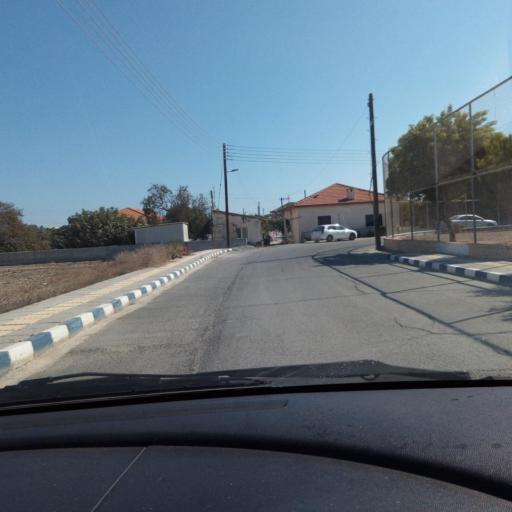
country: CY
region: Larnaka
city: Kolossi
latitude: 34.6017
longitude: 32.9537
